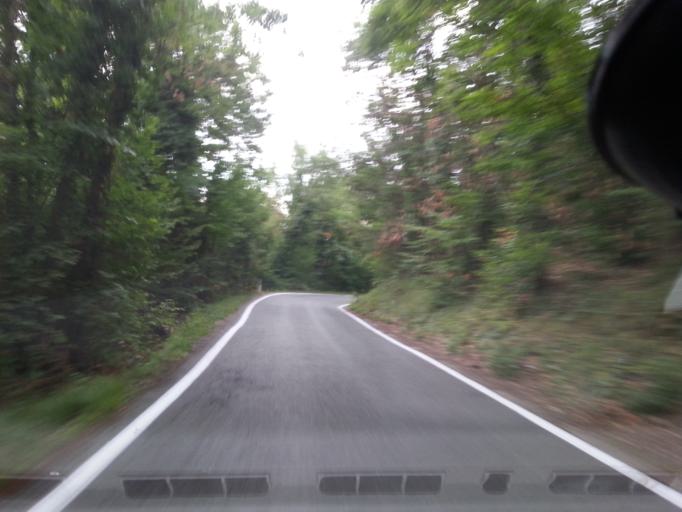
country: IT
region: Piedmont
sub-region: Provincia di Torino
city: Valgioie
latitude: 45.0687
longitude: 7.3630
